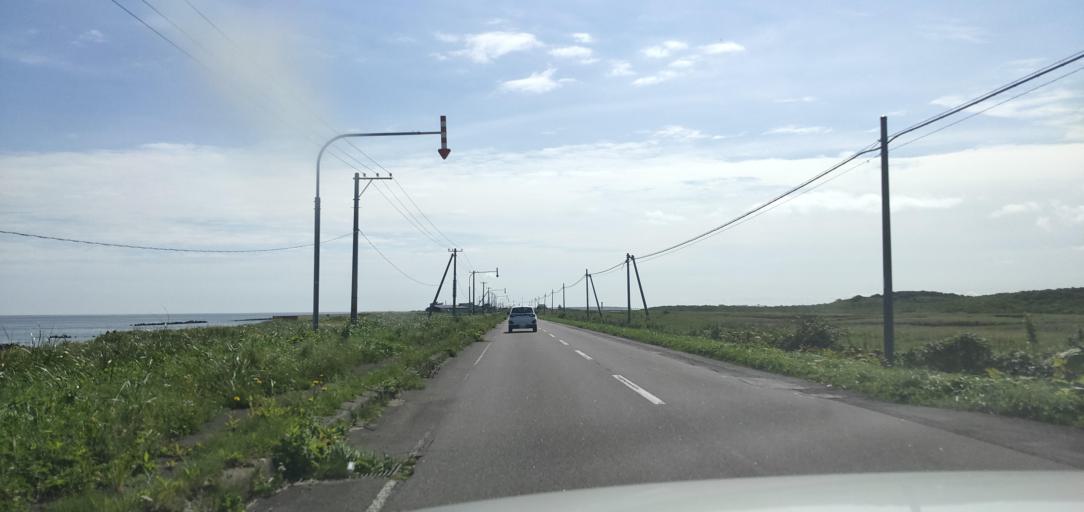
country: JP
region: Hokkaido
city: Shibetsu
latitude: 43.6340
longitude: 145.1789
